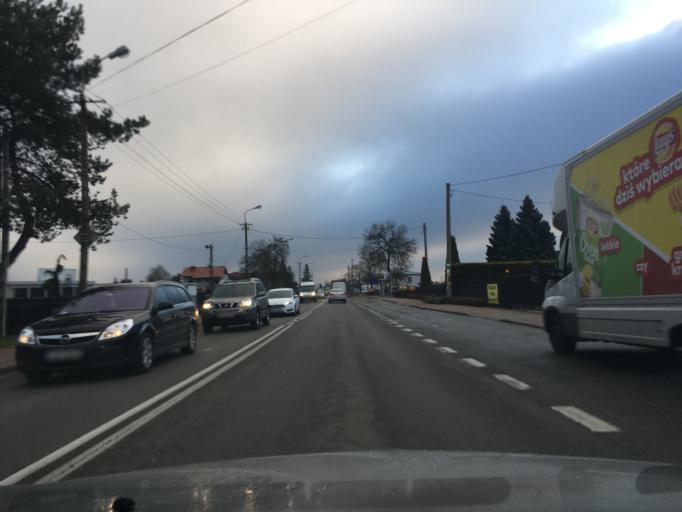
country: PL
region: Masovian Voivodeship
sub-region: Powiat piaseczynski
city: Lesznowola
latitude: 52.0859
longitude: 20.9487
